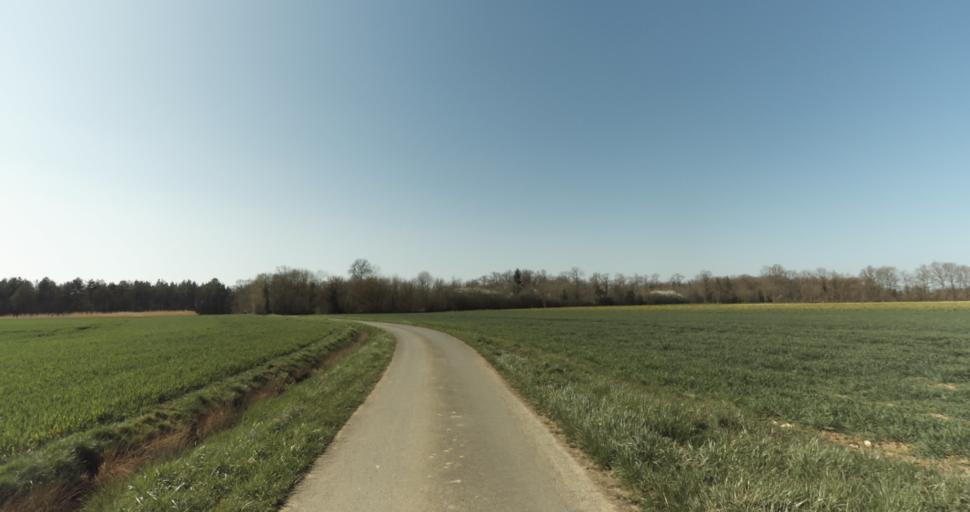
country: FR
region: Lower Normandy
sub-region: Departement du Calvados
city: Saint-Pierre-sur-Dives
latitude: 48.9493
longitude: -0.0293
